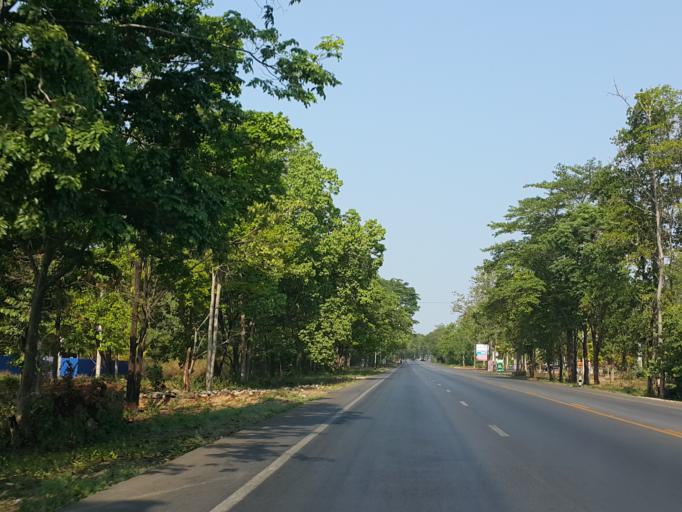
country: TH
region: Kanchanaburi
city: Sai Yok
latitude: 14.1138
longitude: 99.2003
